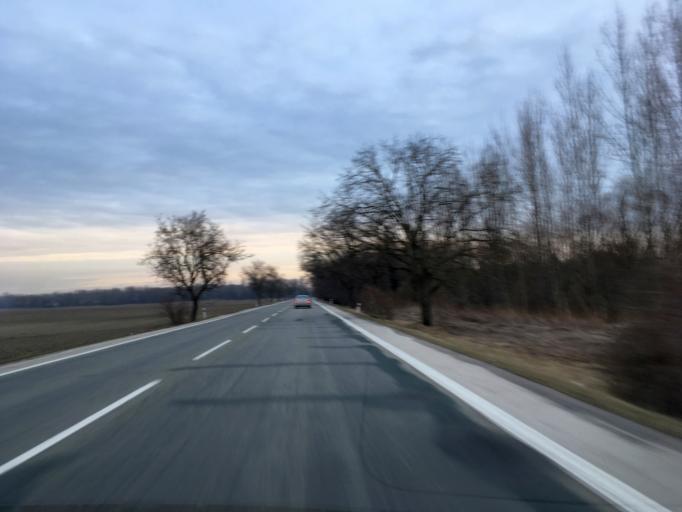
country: SK
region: Trnavsky
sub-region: Okres Dunajska Streda
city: Velky Meder
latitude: 47.9067
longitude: 17.7372
